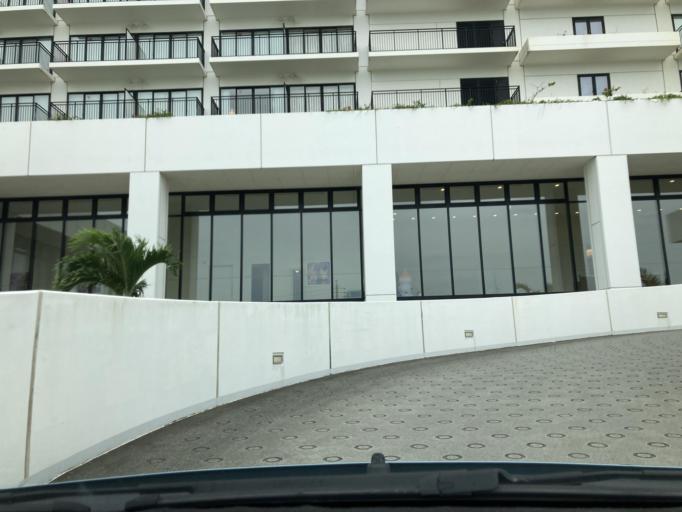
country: JP
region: Okinawa
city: Itoman
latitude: 26.1320
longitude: 127.6533
